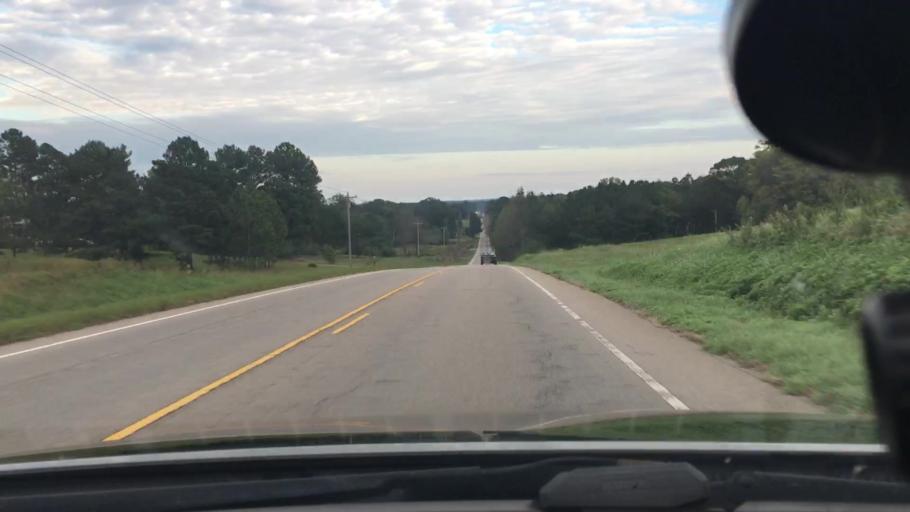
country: US
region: North Carolina
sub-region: Moore County
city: Robbins
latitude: 35.3916
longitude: -79.5177
